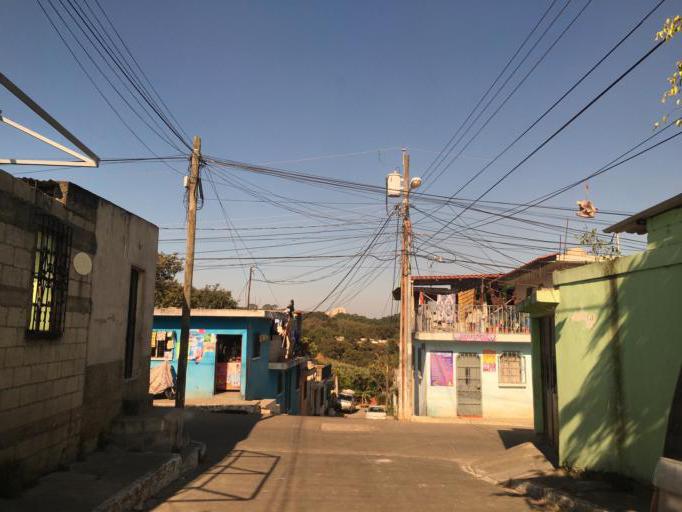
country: GT
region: Guatemala
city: Mixco
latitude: 14.6124
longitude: -90.5733
